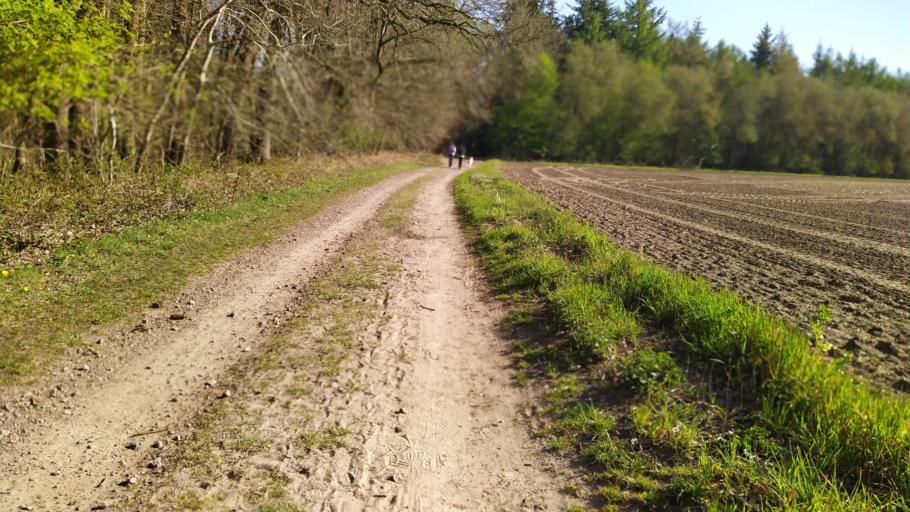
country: DE
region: Lower Saxony
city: Klein Meckelsen
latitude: 53.2982
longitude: 9.4364
